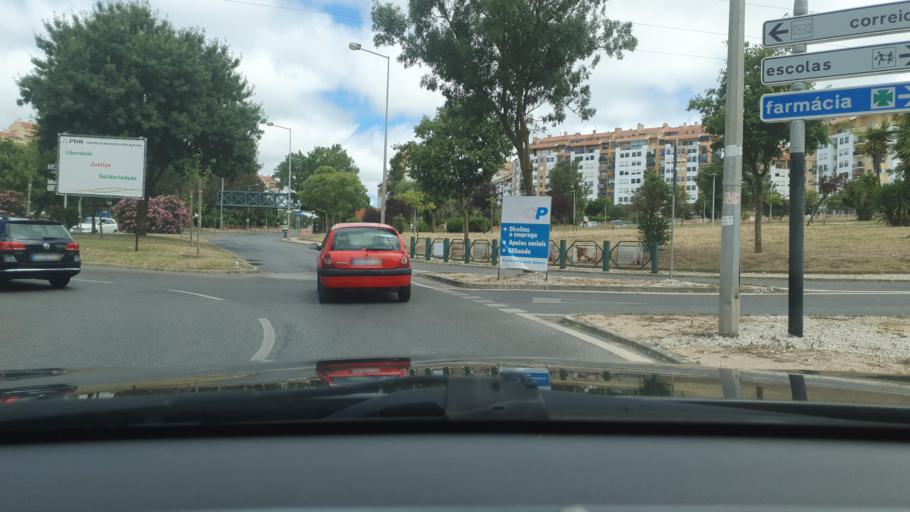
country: PT
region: Lisbon
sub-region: Sintra
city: Cacem
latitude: 38.7615
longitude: -9.2783
